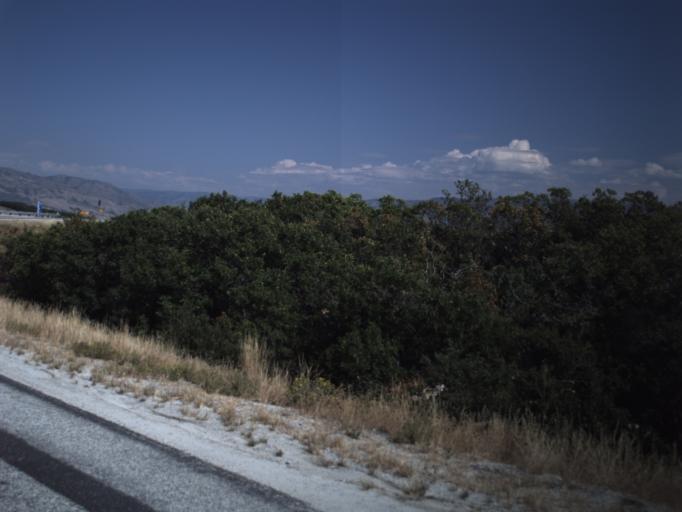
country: US
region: Utah
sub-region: Morgan County
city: Mountain Green
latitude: 41.2064
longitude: -111.8165
